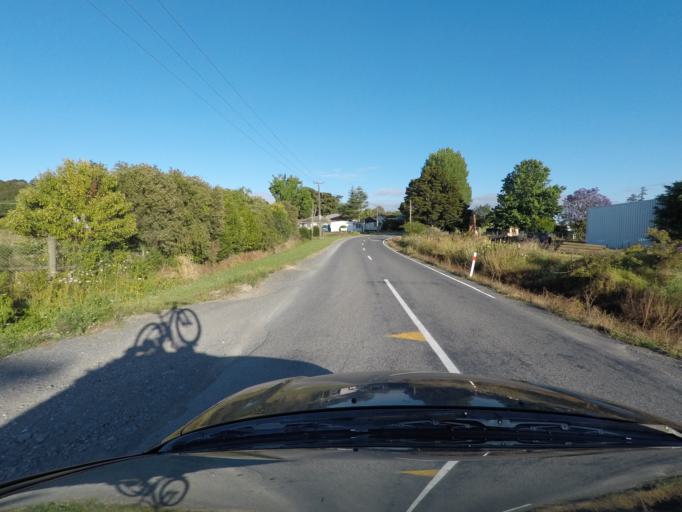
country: NZ
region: Northland
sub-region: Whangarei
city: Whangarei
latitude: -35.6417
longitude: 174.2983
